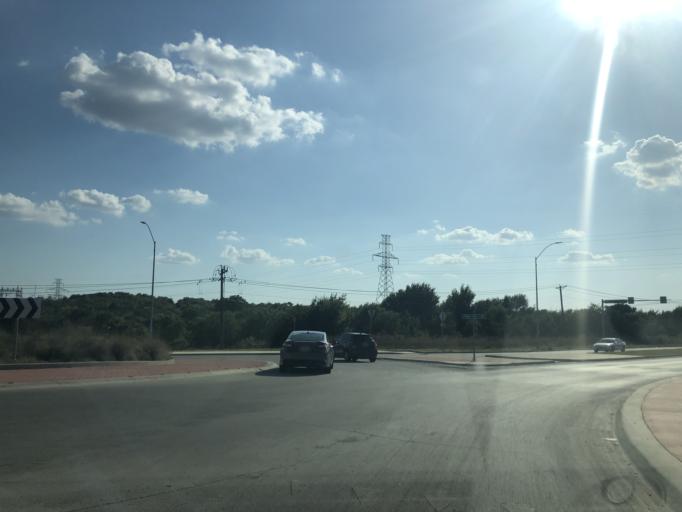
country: US
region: Texas
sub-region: Tarrant County
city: Sansom Park
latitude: 32.8173
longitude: -97.3797
